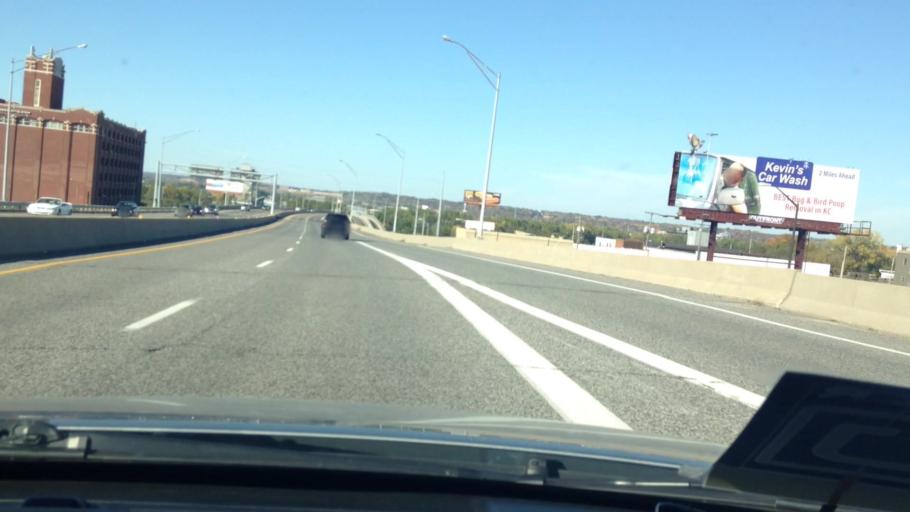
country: US
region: Missouri
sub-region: Jackson County
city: Kansas City
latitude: 39.1093
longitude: -94.5770
